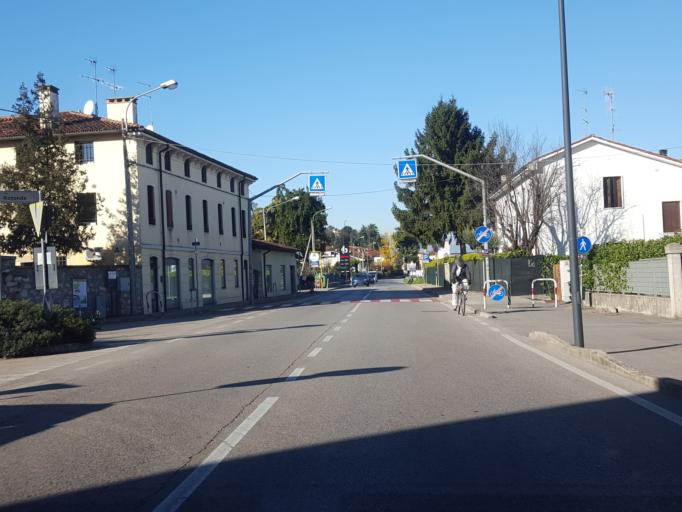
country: IT
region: Veneto
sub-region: Provincia di Vicenza
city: Vicenza
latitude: 45.5344
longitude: 11.5600
